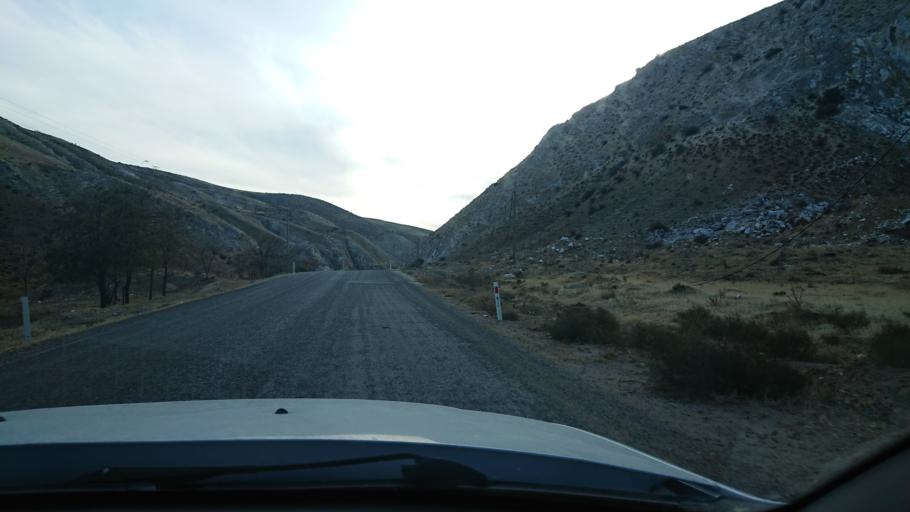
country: TR
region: Ankara
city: Sereflikochisar
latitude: 38.7542
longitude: 33.6927
